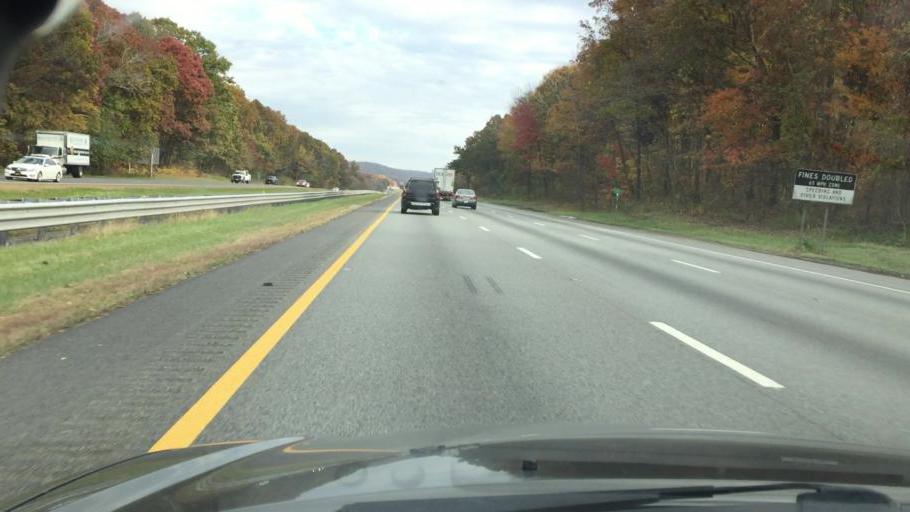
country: US
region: New Jersey
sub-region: Morris County
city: Kenvil
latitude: 40.8999
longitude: -74.6261
